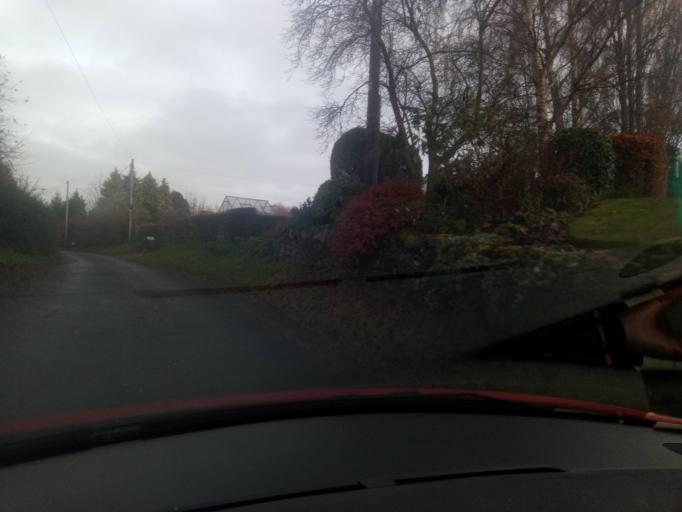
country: GB
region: Scotland
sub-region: The Scottish Borders
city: Jedburgh
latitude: 55.4876
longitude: -2.6034
